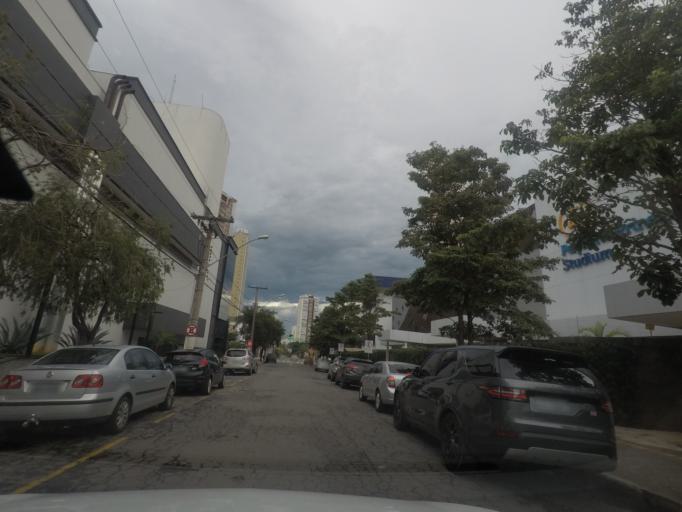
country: BR
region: Goias
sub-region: Goiania
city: Goiania
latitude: -16.6948
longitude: -49.2651
